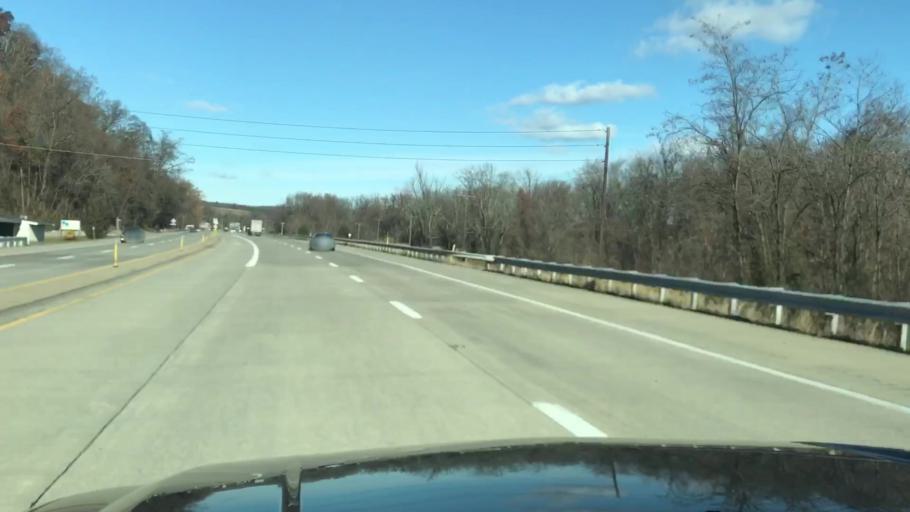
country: US
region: Pennsylvania
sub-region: Dauphin County
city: Millersburg
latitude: 40.5559
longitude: -76.9905
